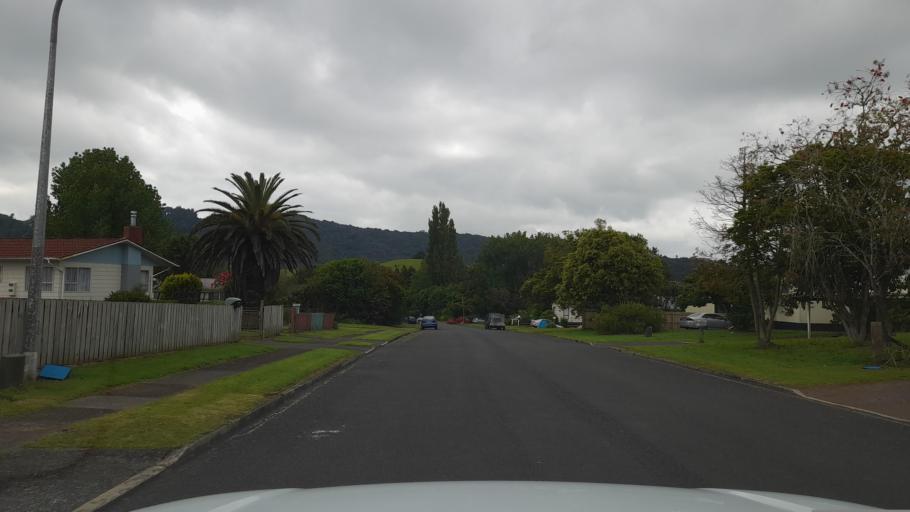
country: NZ
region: Northland
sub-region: Far North District
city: Waimate North
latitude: -35.4024
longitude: 173.7904
